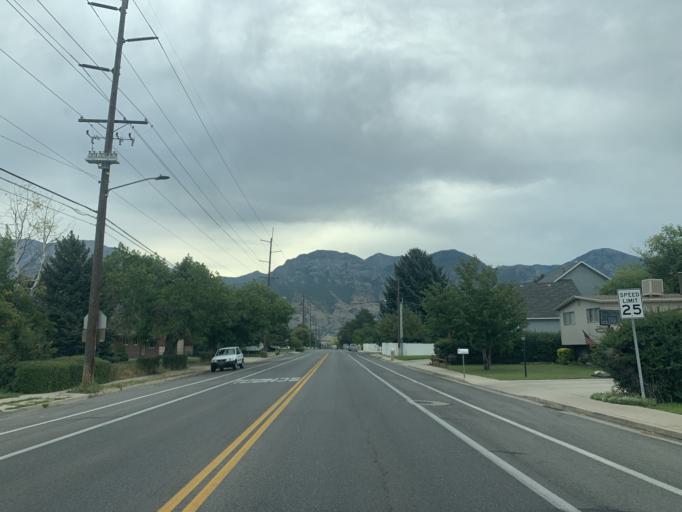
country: US
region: Utah
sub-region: Utah County
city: Provo
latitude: 40.2534
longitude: -111.6846
